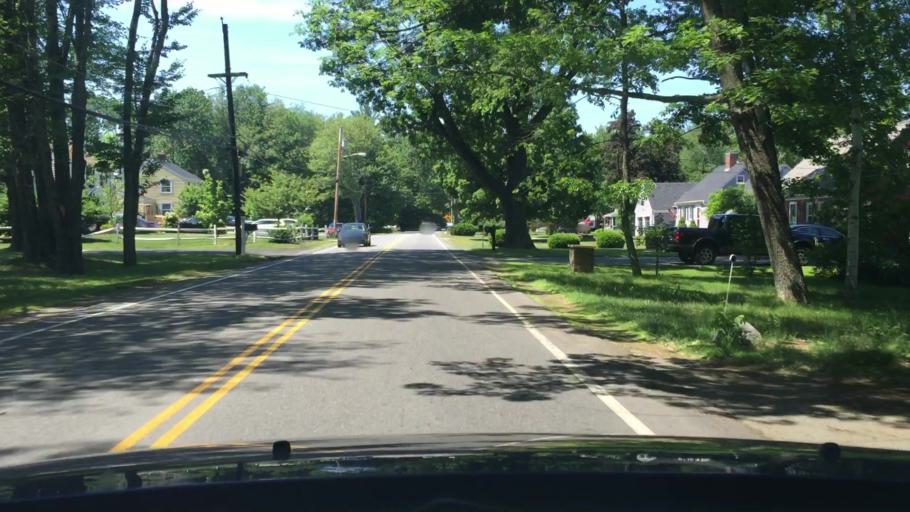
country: US
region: New Hampshire
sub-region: Rockingham County
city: Plaistow
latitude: 42.8154
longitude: -71.0944
